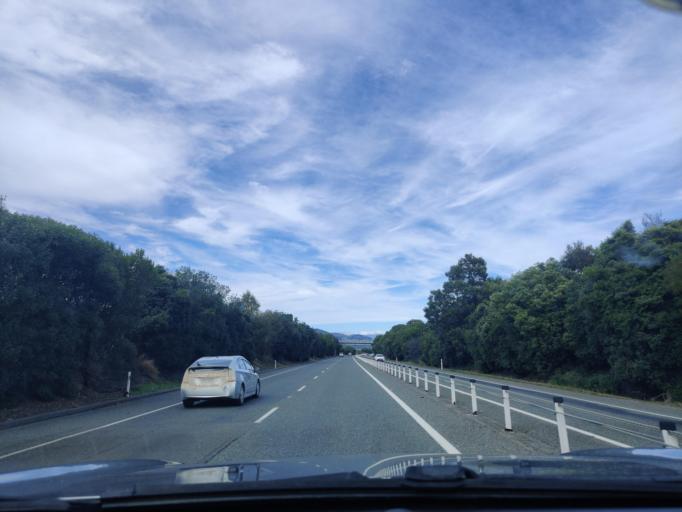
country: NZ
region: Tasman
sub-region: Tasman District
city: Richmond
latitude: -41.3047
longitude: 173.2233
